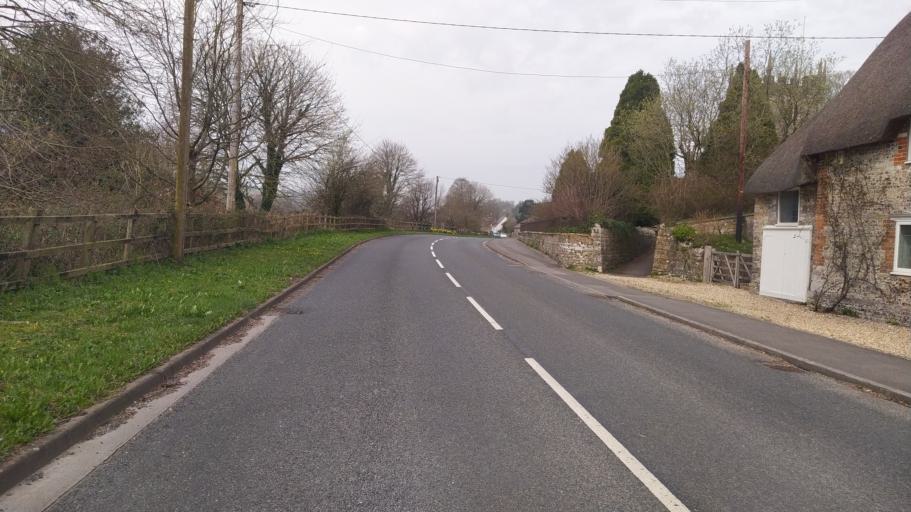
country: GB
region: England
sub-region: Dorset
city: Dorchester
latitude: 50.7527
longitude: -2.5295
